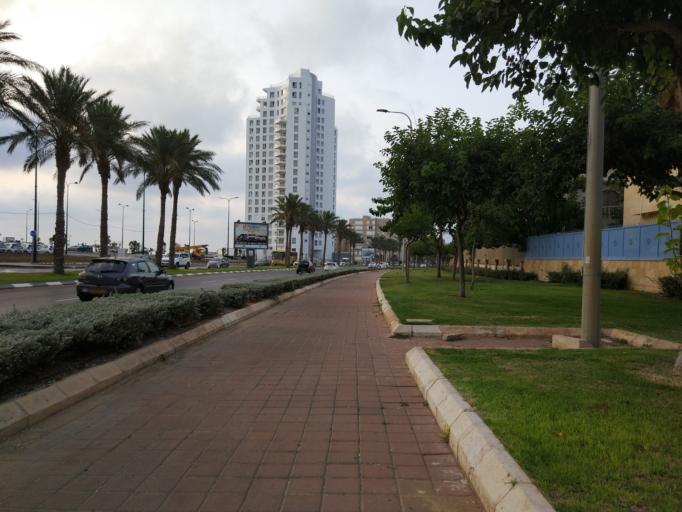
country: IL
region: Central District
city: Netanya
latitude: 32.3172
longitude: 34.8479
